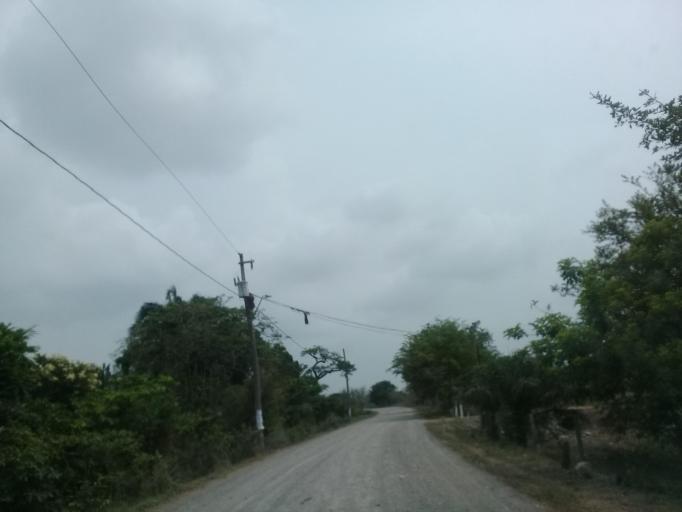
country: MX
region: Veracruz
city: El Tejar
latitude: 19.0586
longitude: -96.1982
